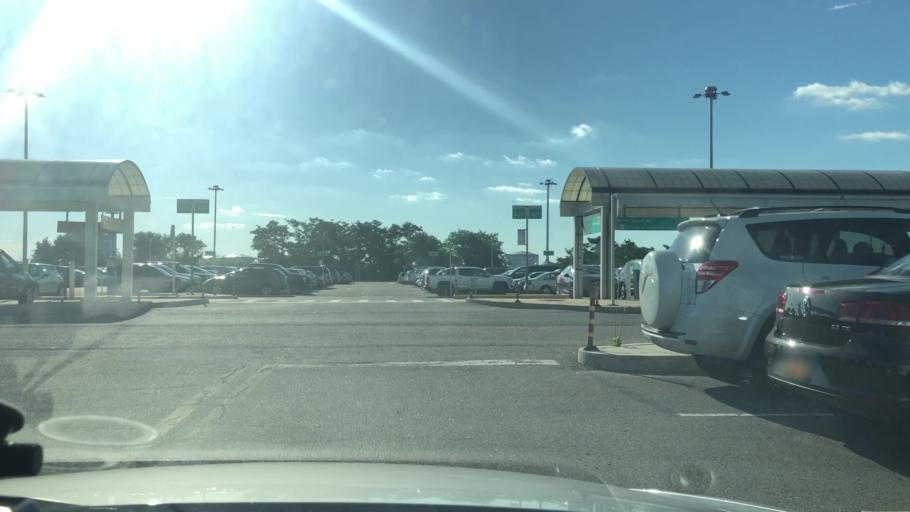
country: US
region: New York
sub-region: Queens County
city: Borough of Queens
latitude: 40.6596
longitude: -73.8263
